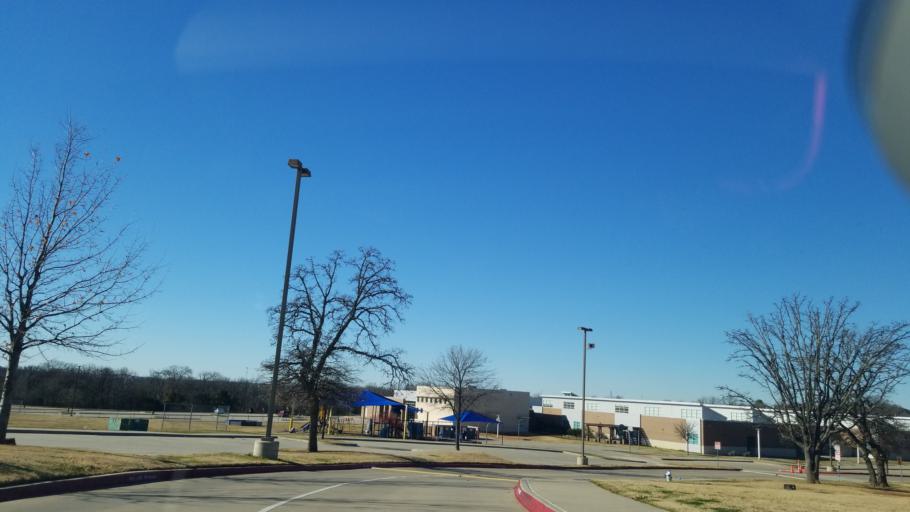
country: US
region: Texas
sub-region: Denton County
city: Corinth
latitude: 33.1468
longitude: -97.0826
